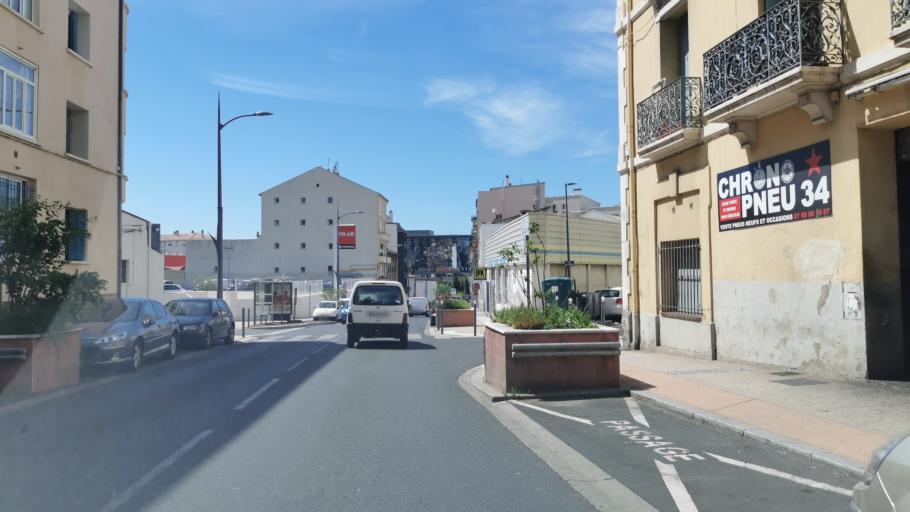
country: FR
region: Languedoc-Roussillon
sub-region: Departement de l'Herault
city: Beziers
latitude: 43.3381
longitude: 3.2253
